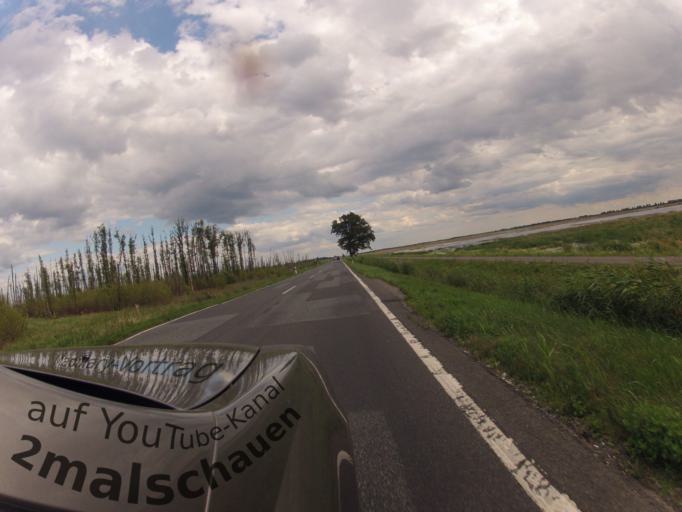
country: DE
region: Mecklenburg-Vorpommern
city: Lassan
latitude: 53.8761
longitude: 13.8035
